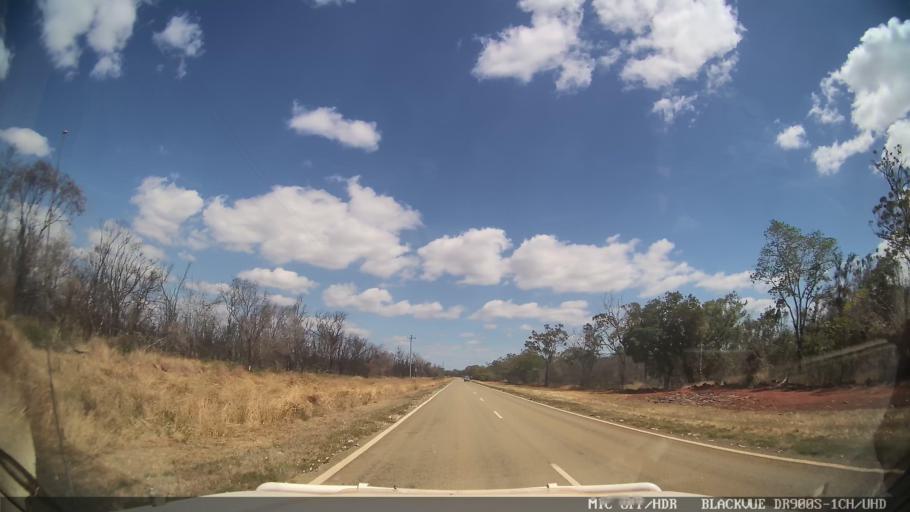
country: AU
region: Queensland
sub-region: Tablelands
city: Ravenshoe
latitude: -18.1286
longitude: 144.8165
